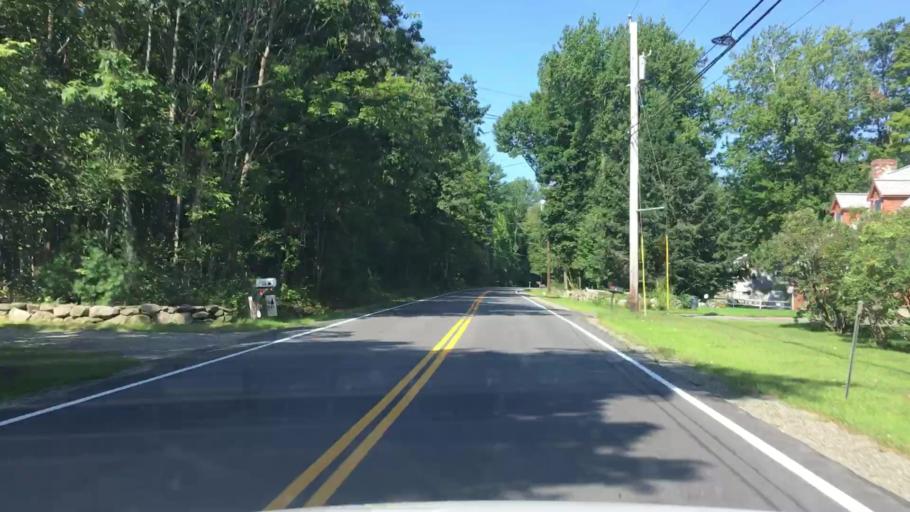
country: US
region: New Hampshire
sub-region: Rockingham County
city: Kensington
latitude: 42.9151
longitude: -70.9699
